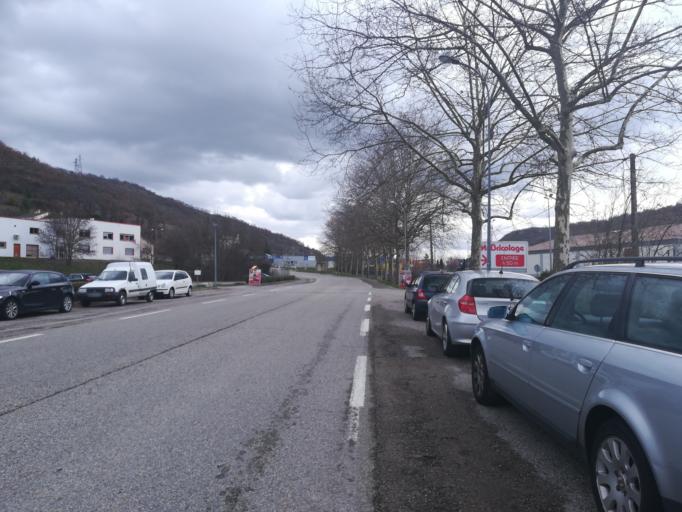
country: FR
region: Rhone-Alpes
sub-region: Departement de l'Ardeche
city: Privas
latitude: 44.7174
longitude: 4.6106
